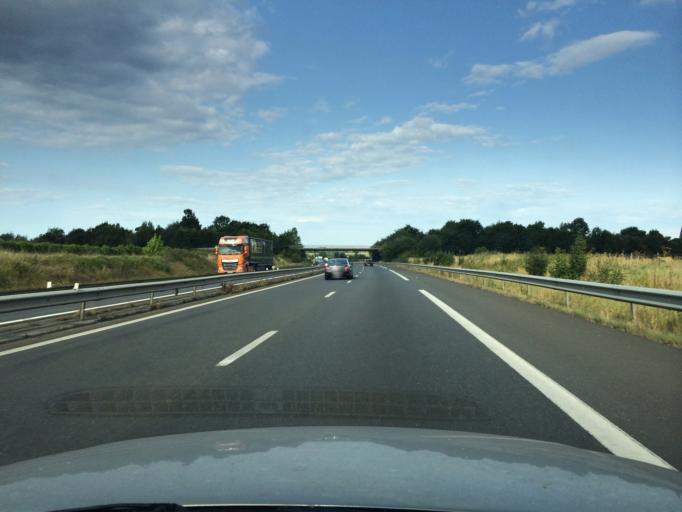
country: FR
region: Lower Normandy
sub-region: Departement du Calvados
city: Sannerville
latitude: 49.1686
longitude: -0.2236
